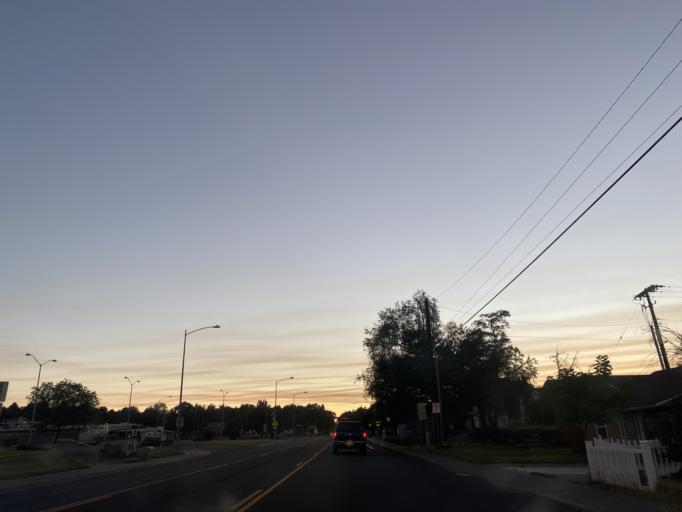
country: US
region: Washington
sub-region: Benton County
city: Kennewick
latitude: 46.1985
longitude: -119.1298
